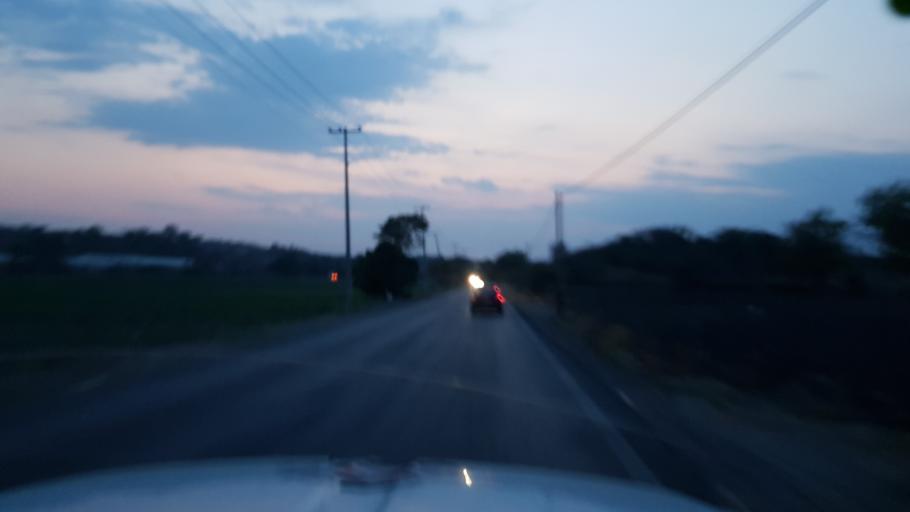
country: MX
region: Morelos
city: Tlaltizapan
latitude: 18.6896
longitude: -99.1357
